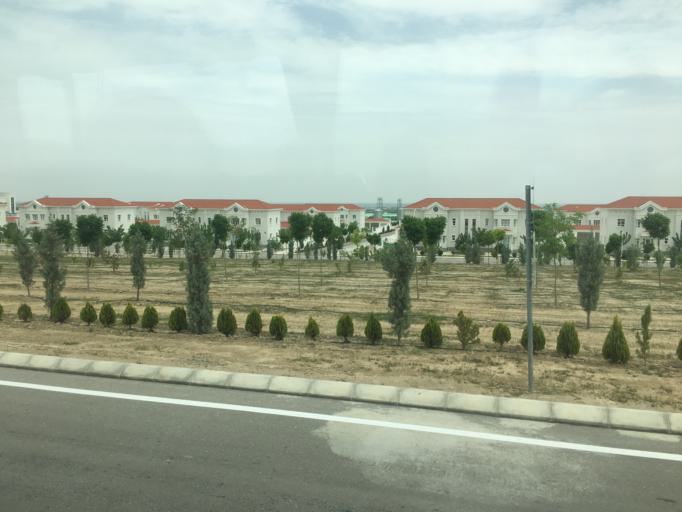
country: TM
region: Ahal
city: Arcabil
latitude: 38.0423
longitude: 58.0357
